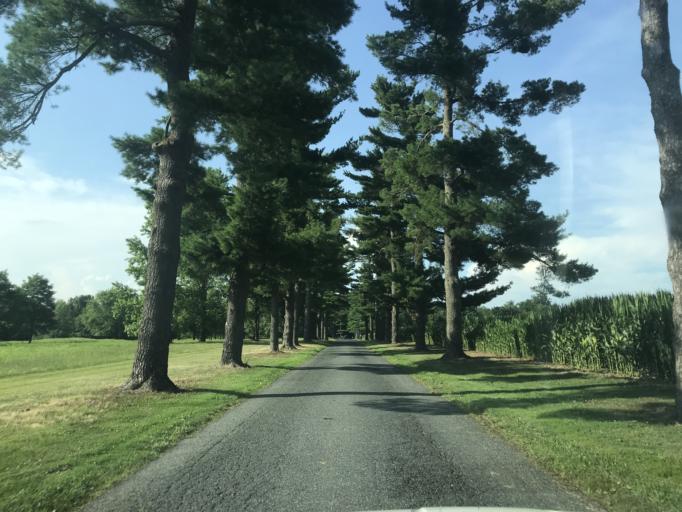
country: US
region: Maryland
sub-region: Harford County
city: Aberdeen
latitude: 39.5091
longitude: -76.1263
